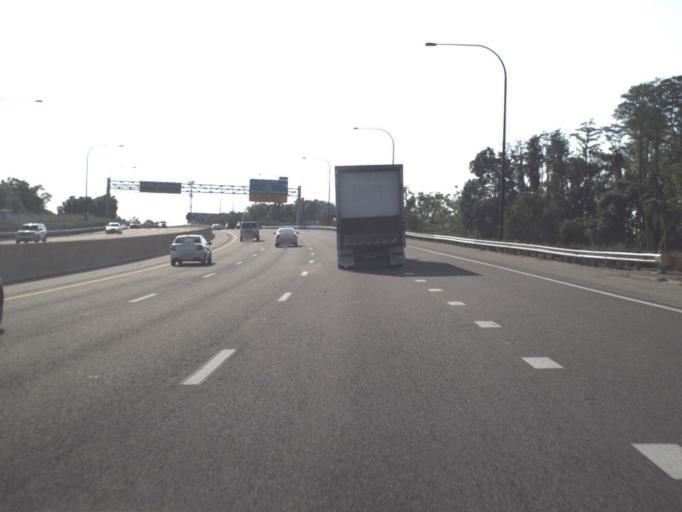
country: US
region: Florida
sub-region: Orange County
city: Pine Hills
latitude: 28.5451
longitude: -81.4172
